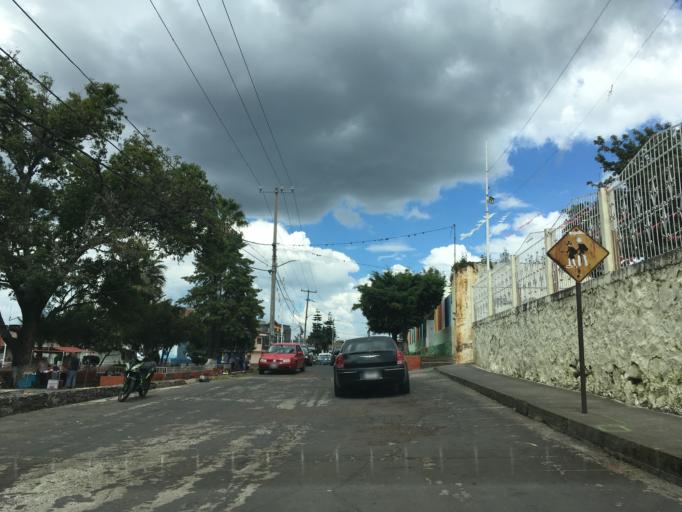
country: MX
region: Michoacan
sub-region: Jimenez
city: Copandaro (Copandaro del Cuatro)
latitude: 19.8215
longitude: -101.6799
